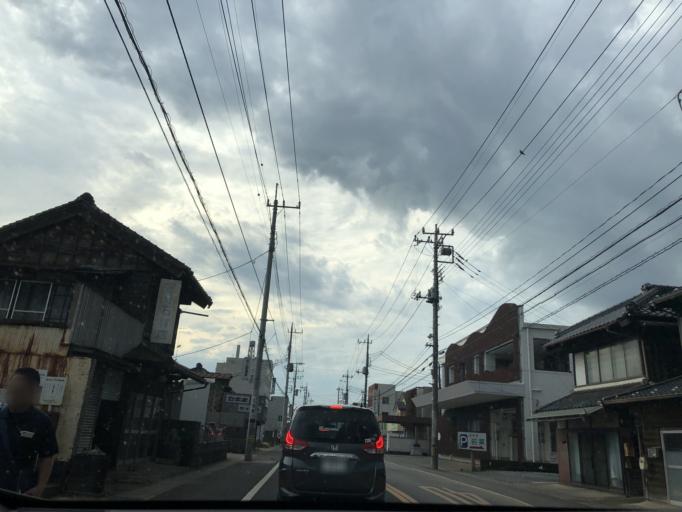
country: JP
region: Tochigi
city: Sano
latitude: 36.3135
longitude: 139.5724
